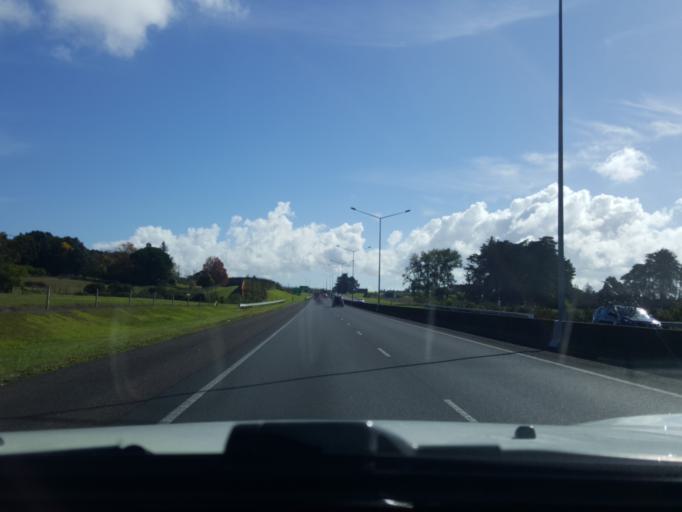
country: NZ
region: Auckland
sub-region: Auckland
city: Rosebank
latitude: -36.8009
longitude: 174.6011
